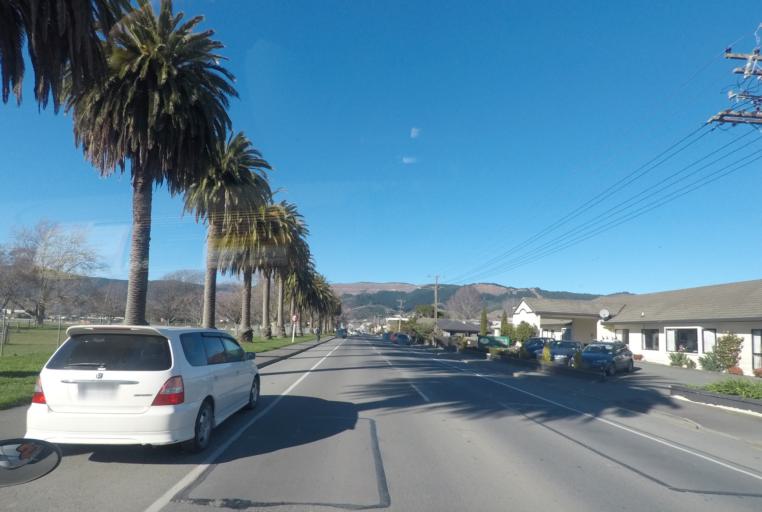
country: NZ
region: Tasman
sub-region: Tasman District
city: Richmond
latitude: -41.3334
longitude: 173.1783
